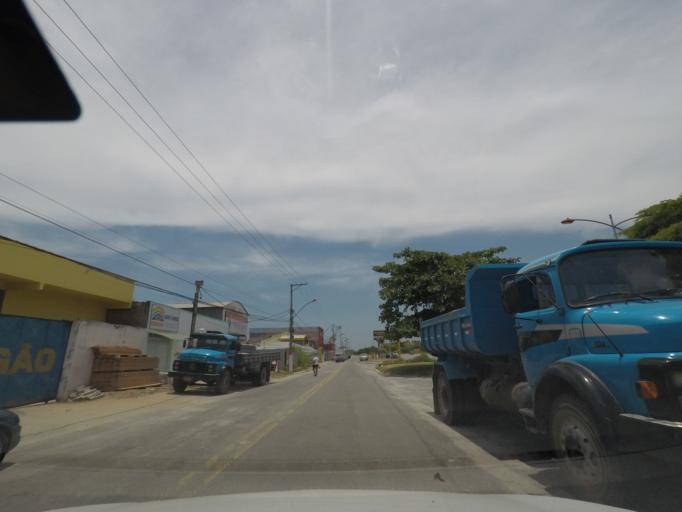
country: BR
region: Rio de Janeiro
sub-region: Marica
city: Marica
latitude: -22.9131
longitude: -42.8444
